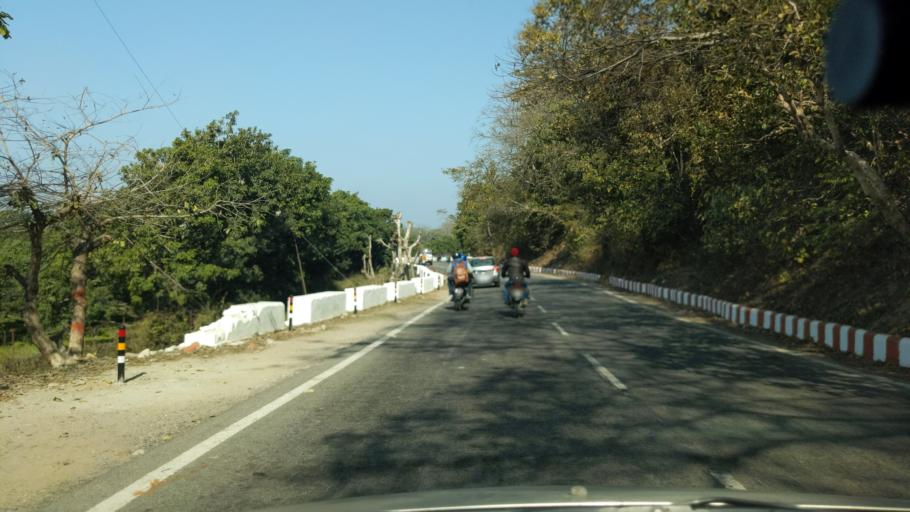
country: IN
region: Uttarakhand
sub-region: Naini Tal
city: Ramnagar
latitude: 29.3871
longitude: 79.1410
